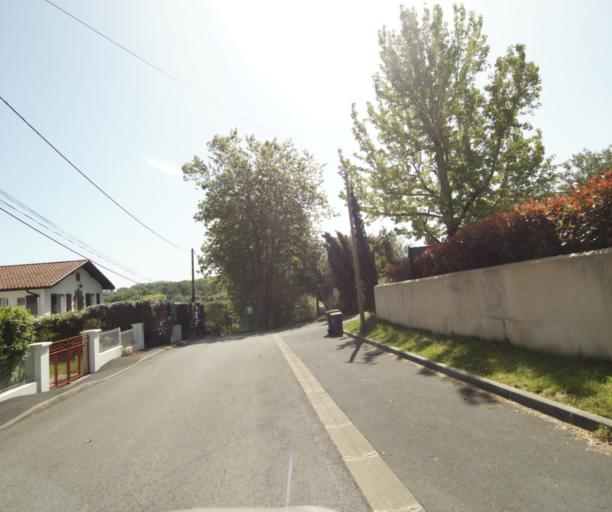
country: FR
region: Aquitaine
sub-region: Departement des Pyrenees-Atlantiques
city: Mouguerre
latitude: 43.4728
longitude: -1.4465
